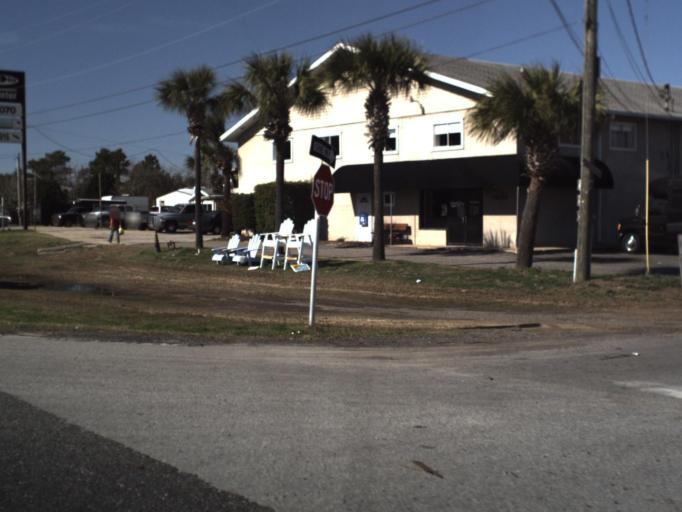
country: US
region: Florida
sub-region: Bay County
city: Laguna Beach
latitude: 30.2408
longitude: -85.9133
